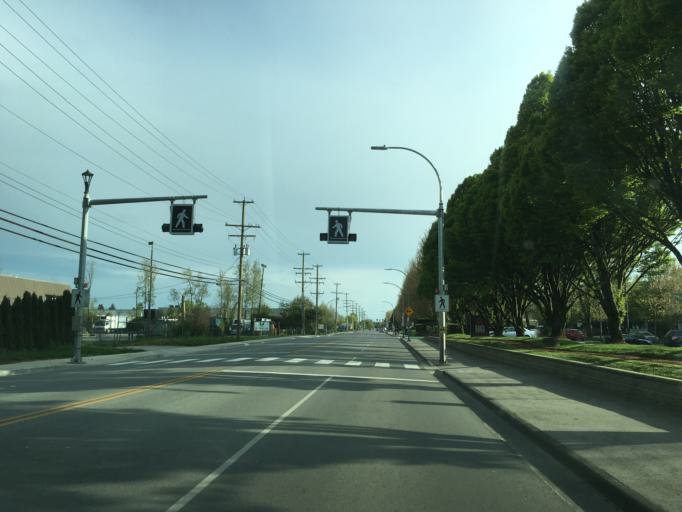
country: CA
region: British Columbia
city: Richmond
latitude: 49.1747
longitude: -123.0693
